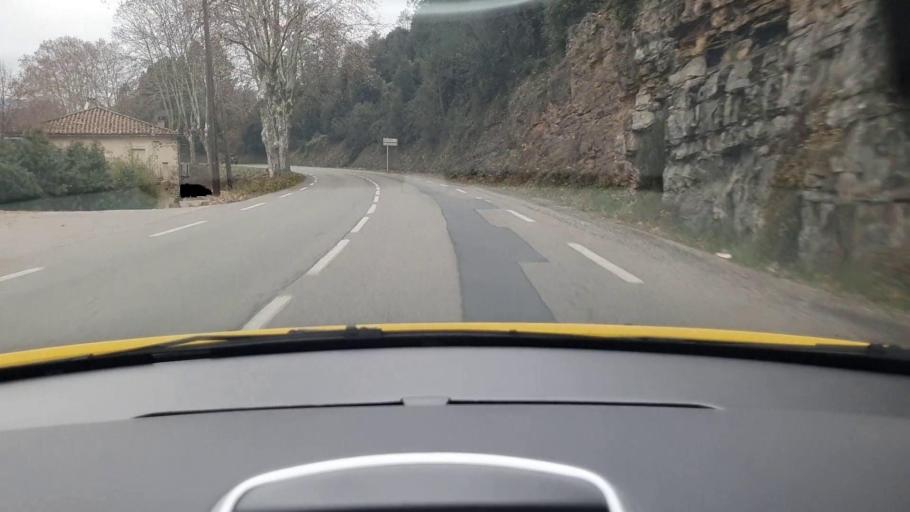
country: FR
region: Languedoc-Roussillon
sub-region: Departement du Gard
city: Saint-Ambroix
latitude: 44.2723
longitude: 4.1904
